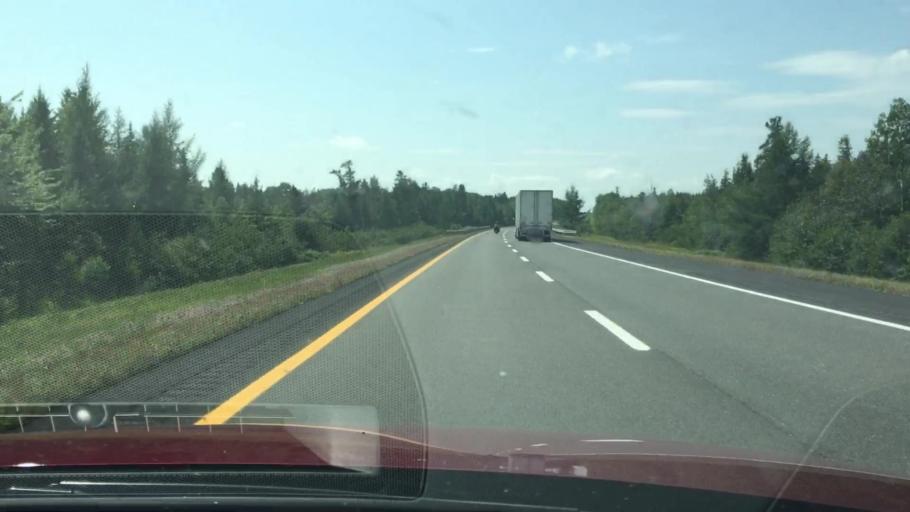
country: US
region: Maine
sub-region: Penobscot County
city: Patten
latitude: 45.9678
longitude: -68.3036
